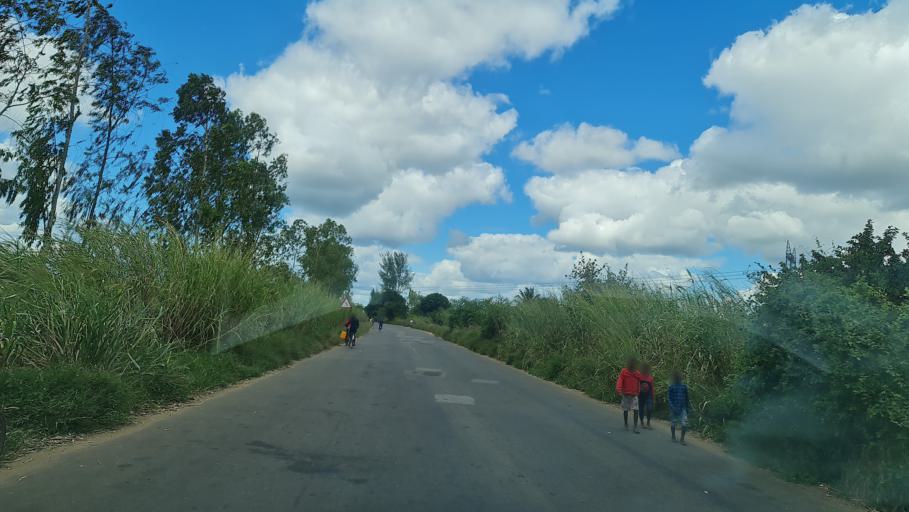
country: MZ
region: Zambezia
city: Quelimane
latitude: -17.5229
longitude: 36.2668
